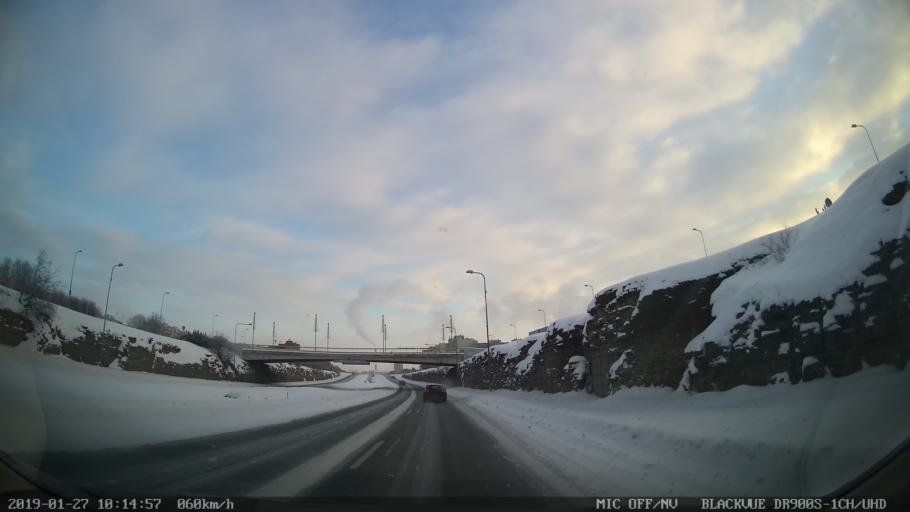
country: EE
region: Harju
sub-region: Tallinna linn
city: Kose
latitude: 59.4431
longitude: 24.8804
